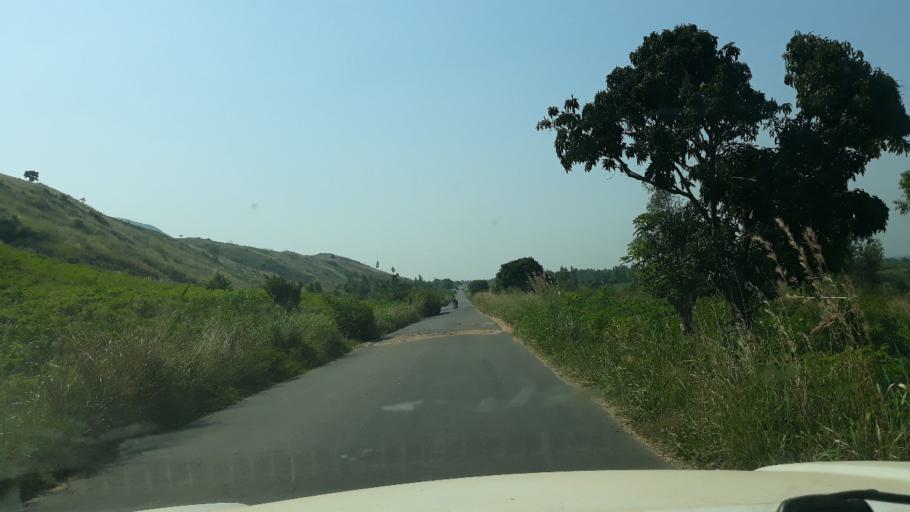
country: CD
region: South Kivu
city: Uvira
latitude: -3.2747
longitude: 29.1608
